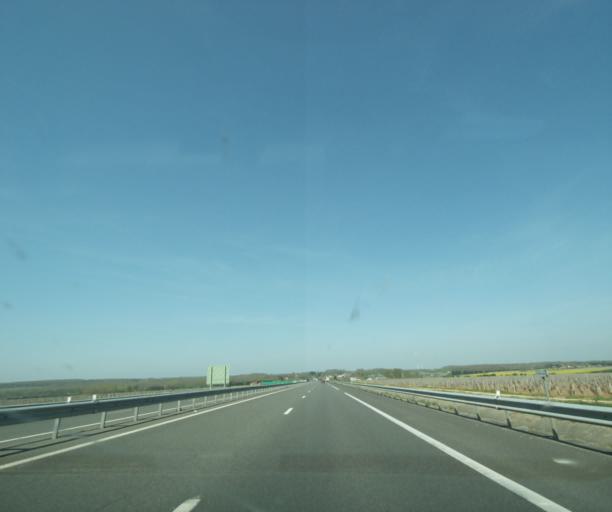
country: FR
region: Bourgogne
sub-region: Departement de la Nievre
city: Pouilly-sur-Loire
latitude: 47.3240
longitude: 2.9336
